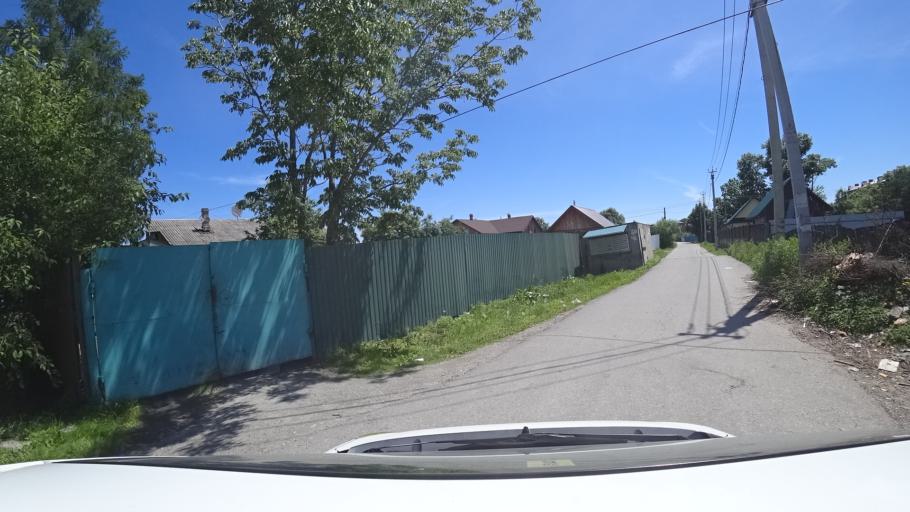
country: RU
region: Khabarovsk Krai
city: Topolevo
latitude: 48.5086
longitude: 135.1788
